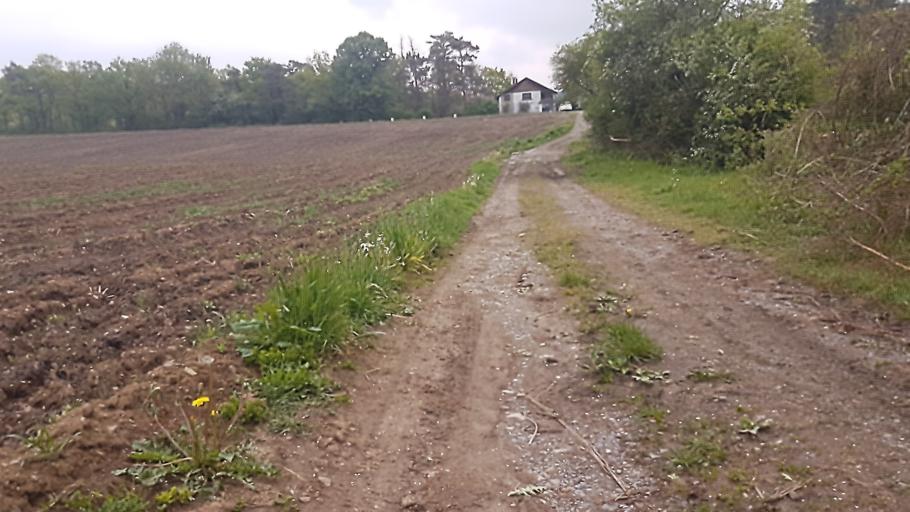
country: BE
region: Wallonia
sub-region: Province de Namur
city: Couvin
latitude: 50.0790
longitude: 4.6063
